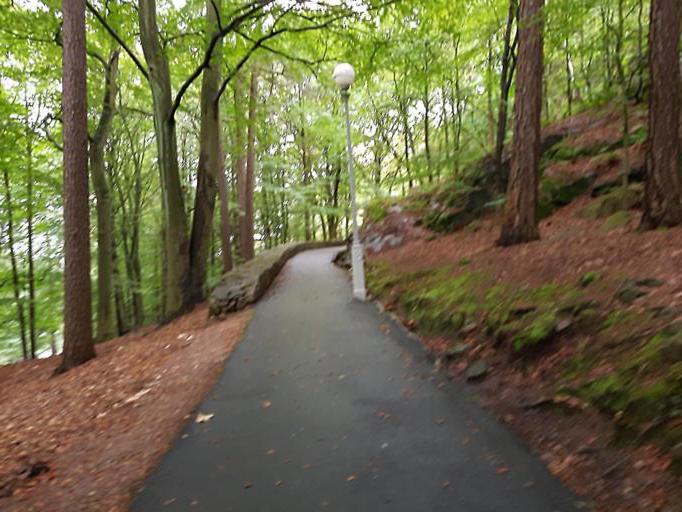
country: SE
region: Vaestra Goetaland
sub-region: Goteborg
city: Goeteborg
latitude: 57.7147
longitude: 11.9398
